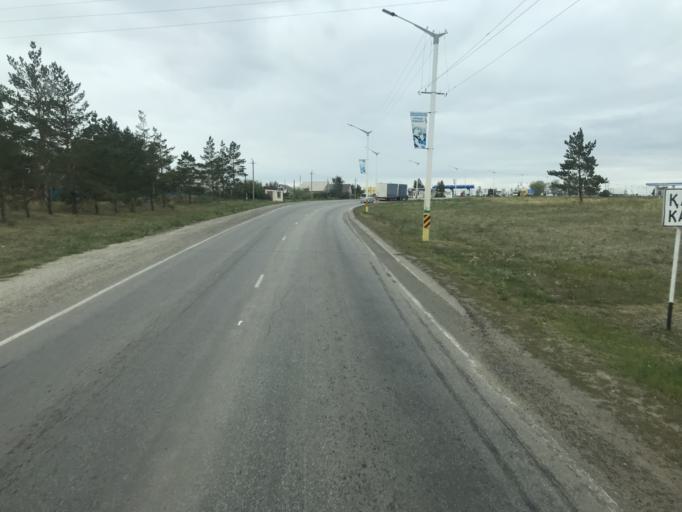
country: KZ
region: Qostanay
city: Komsomolets
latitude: 53.7611
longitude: 62.0758
